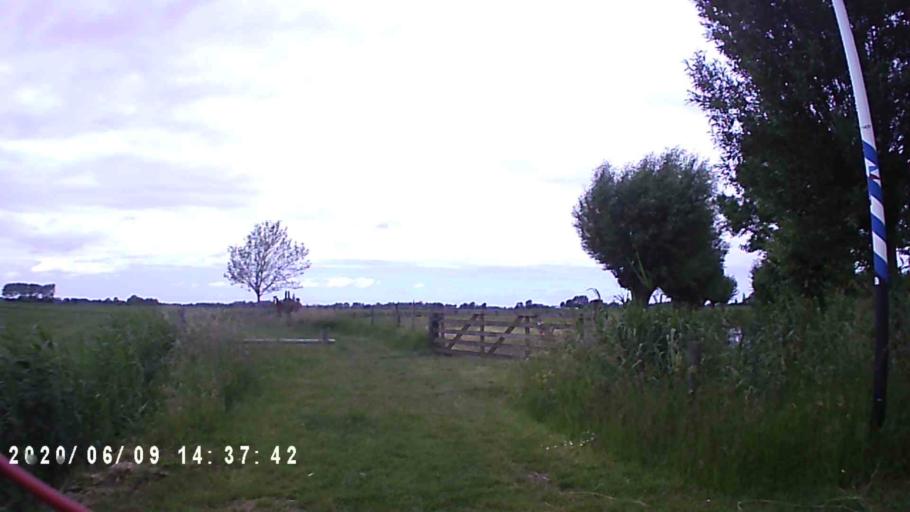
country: NL
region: Groningen
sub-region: Gemeente Bedum
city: Bedum
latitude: 53.3283
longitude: 6.5777
